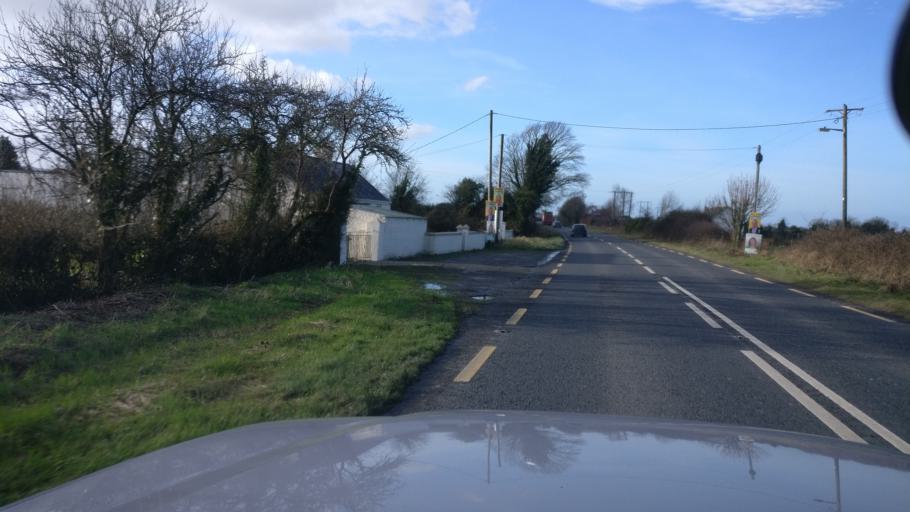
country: IE
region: Leinster
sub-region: Laois
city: Mountmellick
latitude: 53.1254
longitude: -7.3394
